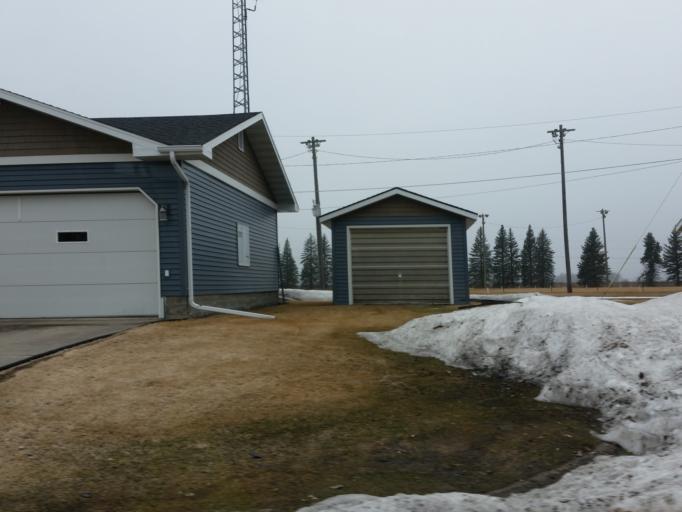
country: US
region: North Dakota
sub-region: Walsh County
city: Grafton
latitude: 48.5580
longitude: -97.1833
